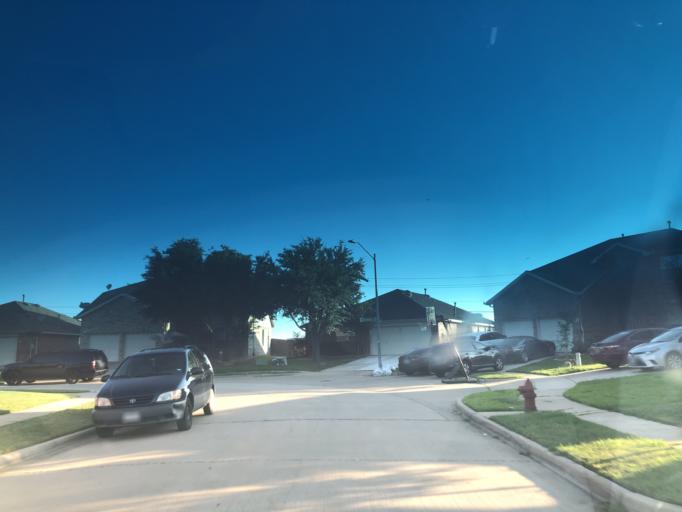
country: US
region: Texas
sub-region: Dallas County
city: Grand Prairie
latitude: 32.7046
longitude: -97.0205
